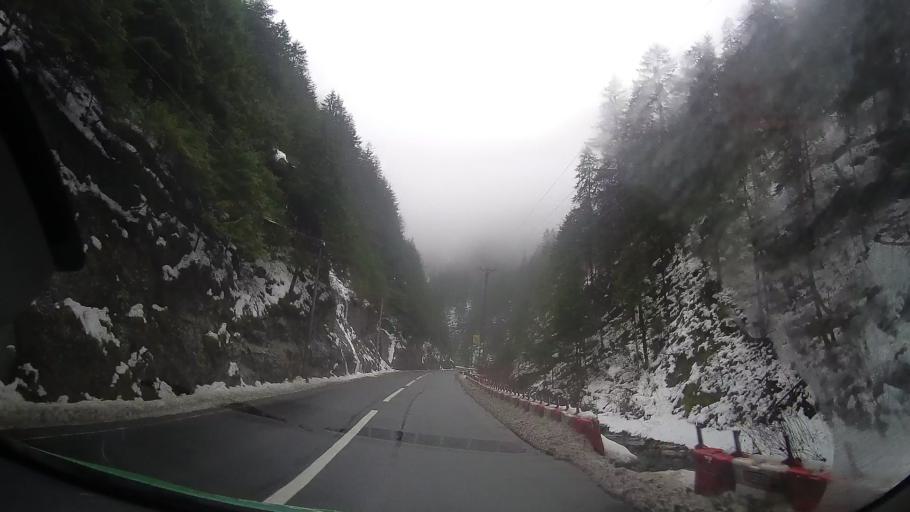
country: RO
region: Neamt
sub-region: Comuna Bicaz Chei
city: Bicaz Chei
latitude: 46.8028
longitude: 25.8038
